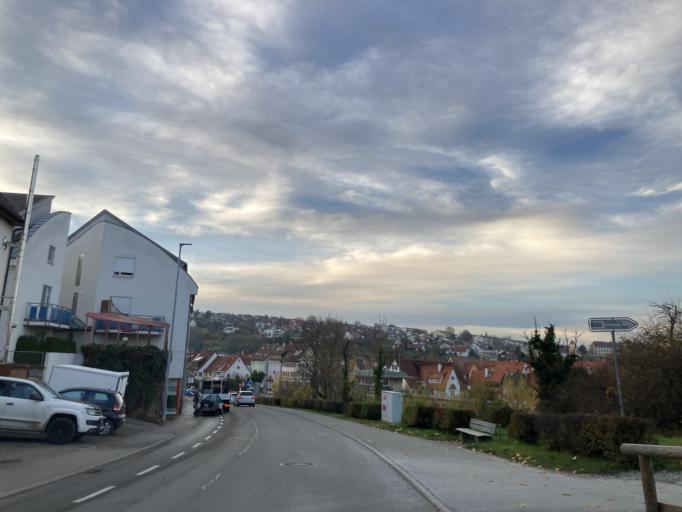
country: DE
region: Baden-Wuerttemberg
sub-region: Tuebingen Region
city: Rottenburg
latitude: 48.4718
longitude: 8.9345
